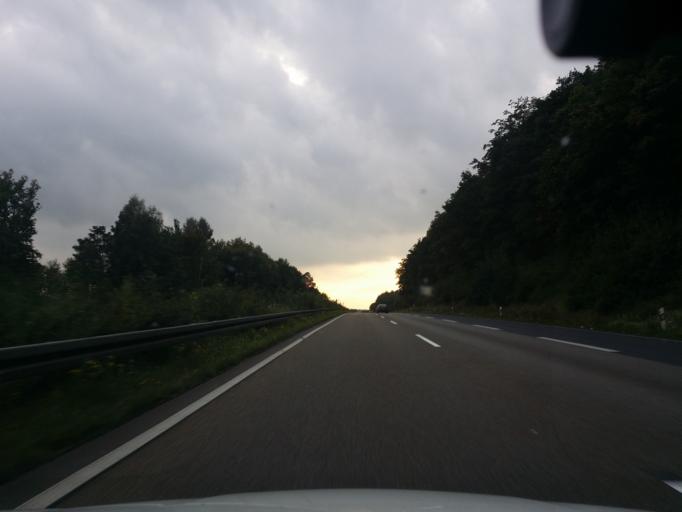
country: DE
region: Hesse
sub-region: Regierungsbezirk Kassel
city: Ottrau
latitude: 50.7581
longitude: 9.3542
